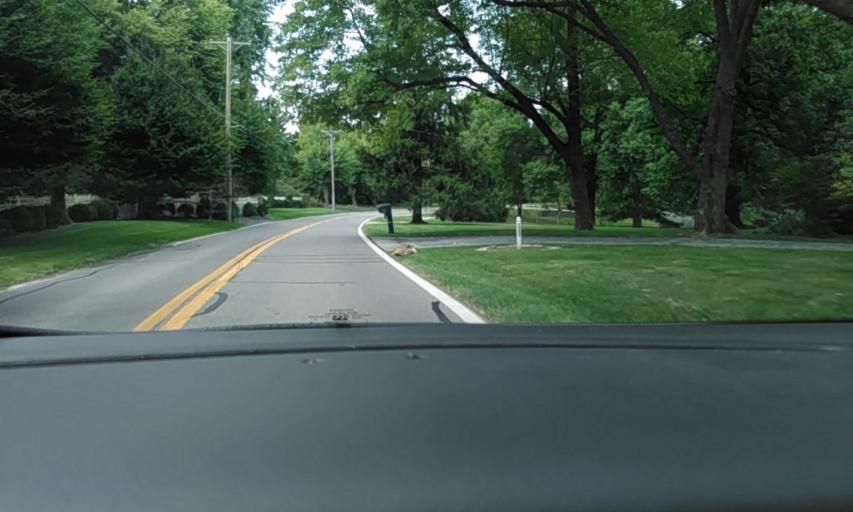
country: US
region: Missouri
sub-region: Saint Louis County
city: Town and Country
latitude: 38.6048
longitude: -90.4847
